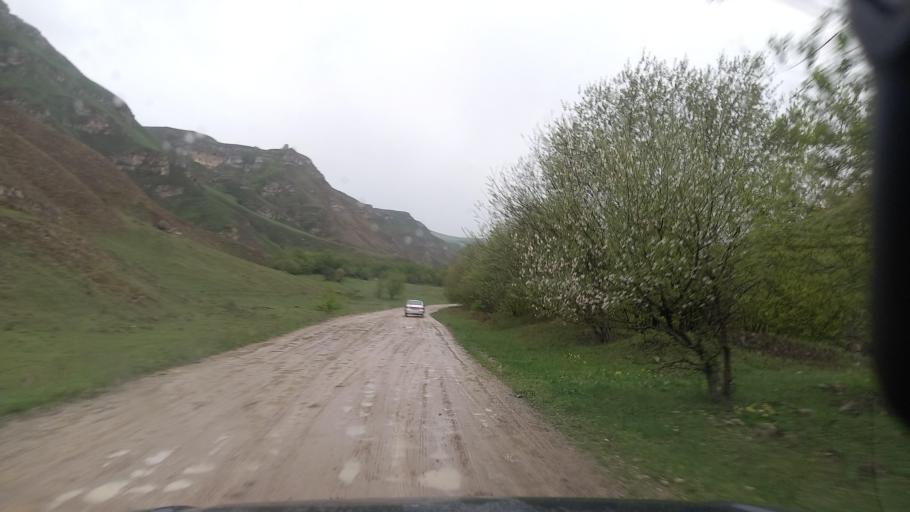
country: RU
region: Kabardino-Balkariya
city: Gundelen
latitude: 43.5983
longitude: 43.0434
